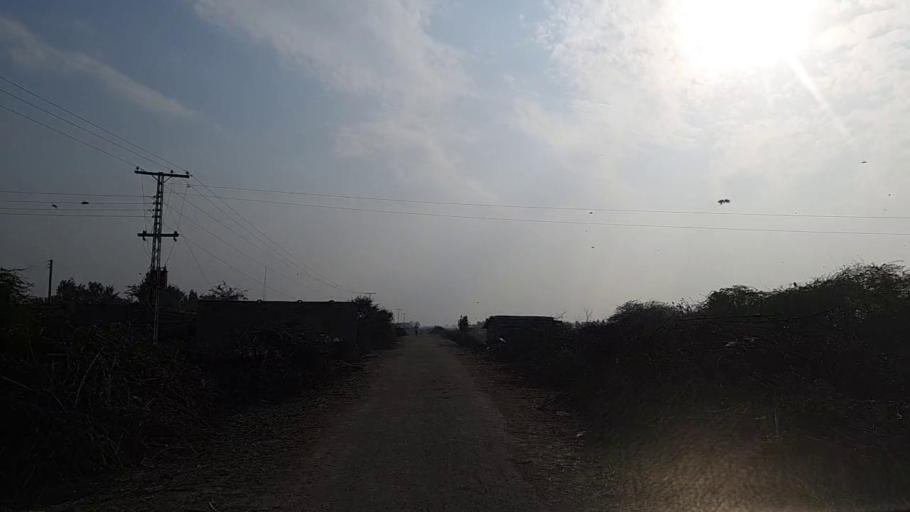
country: PK
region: Sindh
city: Jam Sahib
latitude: 26.3203
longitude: 68.5287
